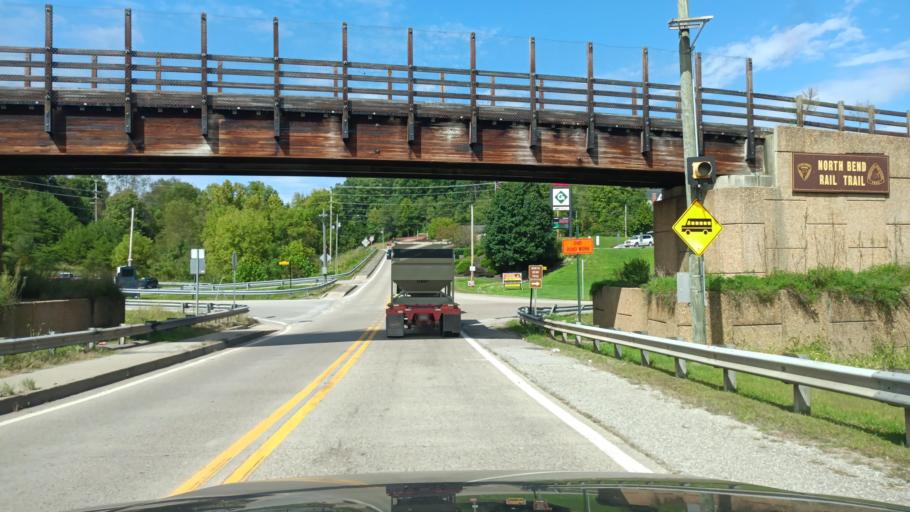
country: US
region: West Virginia
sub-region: Ritchie County
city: Harrisville
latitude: 39.2653
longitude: -81.0564
